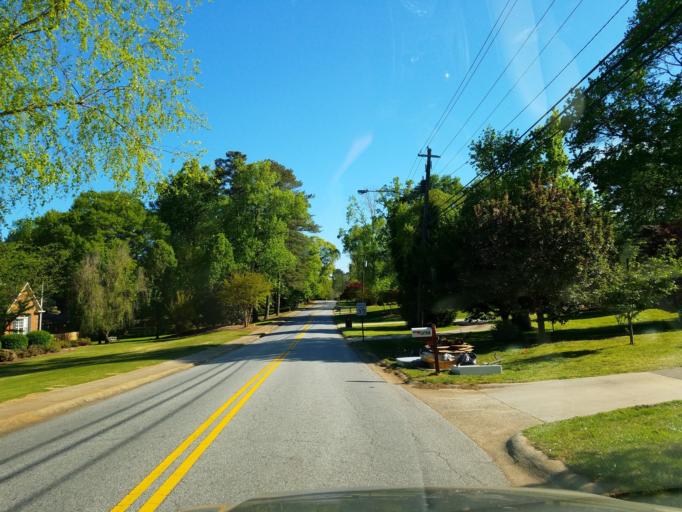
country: US
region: Georgia
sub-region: Cobb County
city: Smyrna
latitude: 33.8627
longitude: -84.5367
